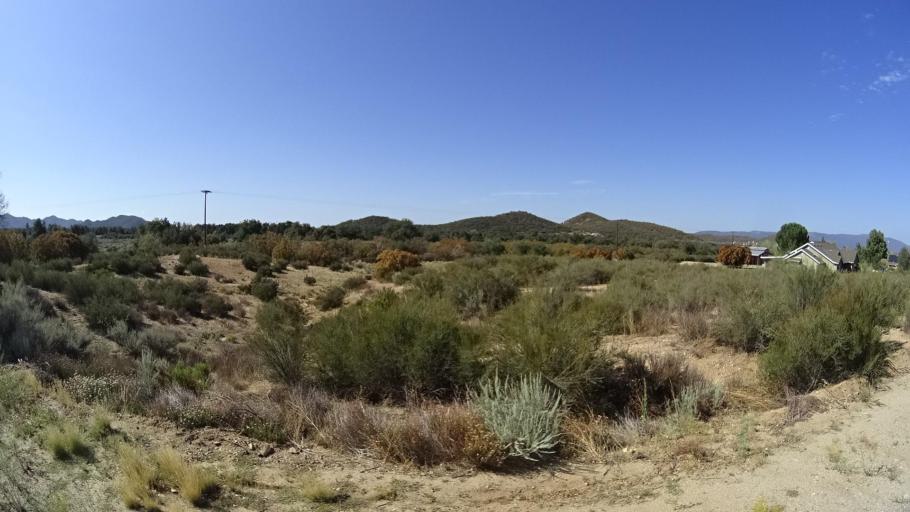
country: US
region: California
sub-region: Riverside County
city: Anza
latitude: 33.3855
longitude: -116.6619
